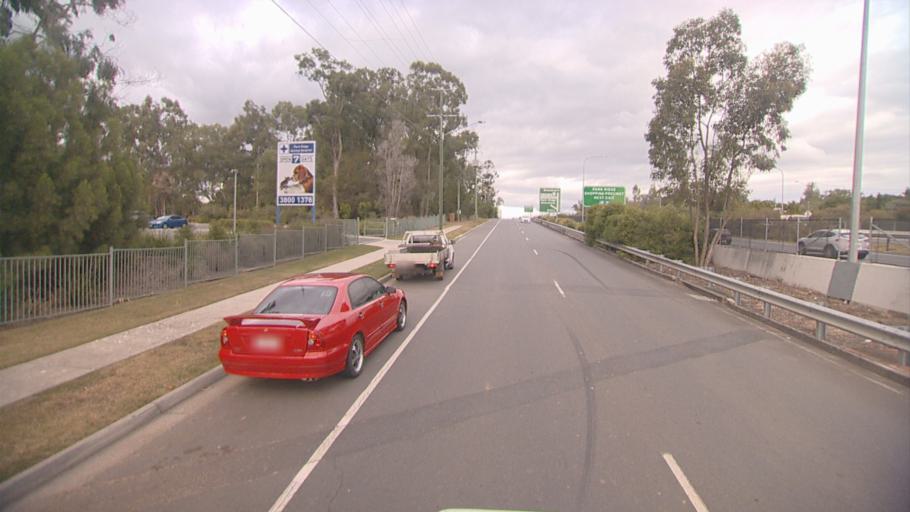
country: AU
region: Queensland
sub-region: Logan
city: Park Ridge South
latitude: -27.6894
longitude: 153.0334
